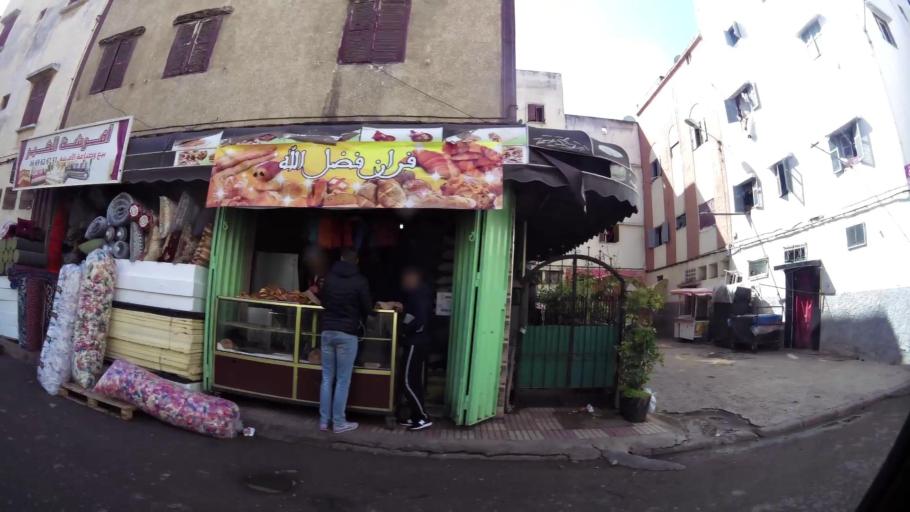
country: MA
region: Grand Casablanca
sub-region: Casablanca
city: Casablanca
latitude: 33.5698
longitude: -7.6769
